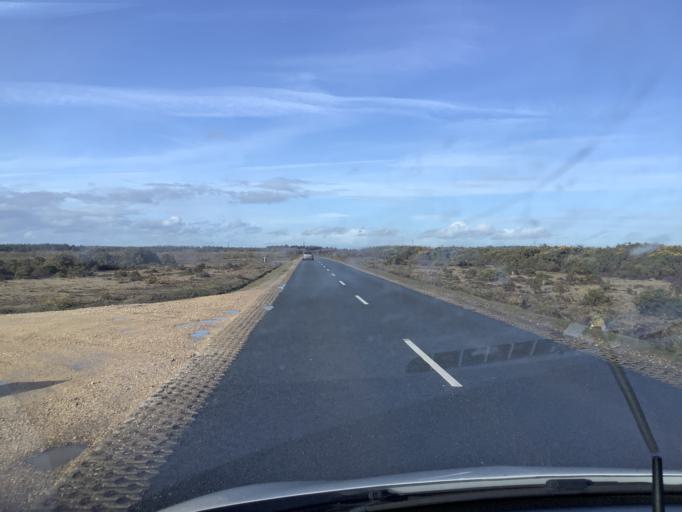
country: GB
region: England
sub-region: Hampshire
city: Hythe
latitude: 50.8326
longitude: -1.4297
